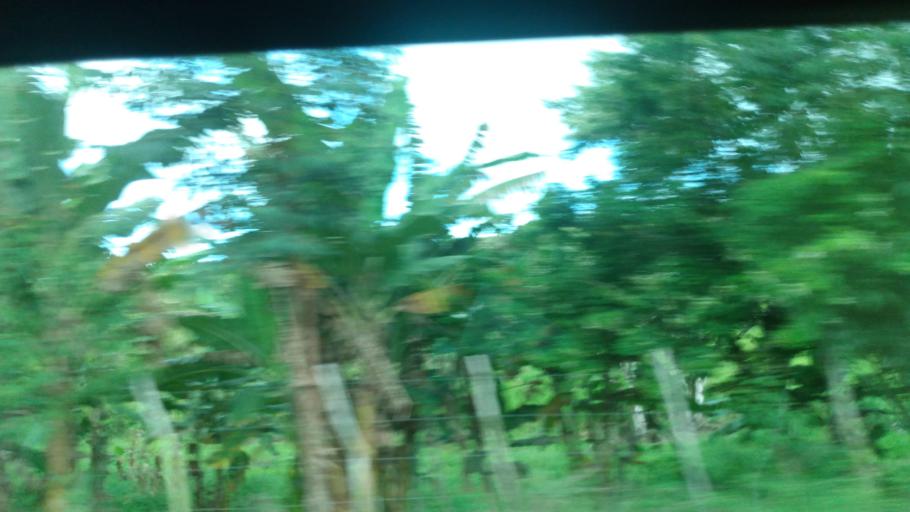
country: BR
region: Pernambuco
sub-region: Quipapa
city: Quipapa
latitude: -8.7882
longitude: -35.9777
